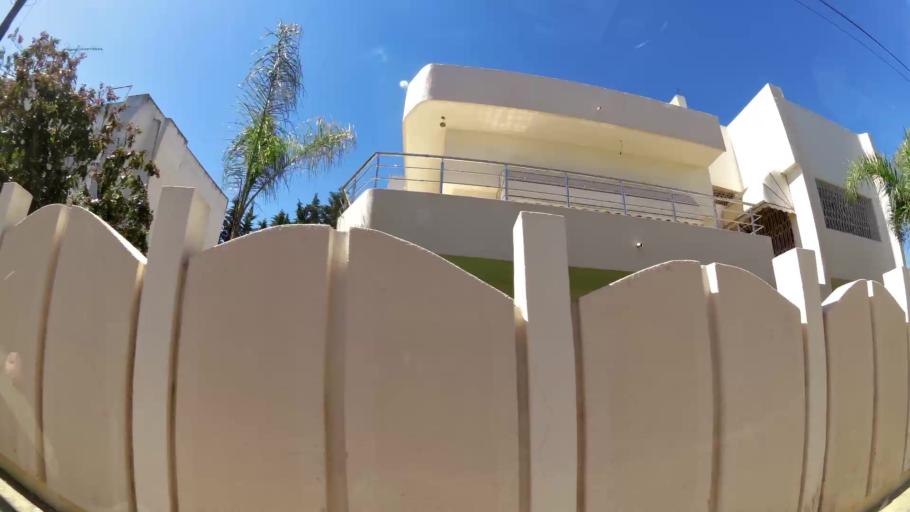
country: MA
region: Fes-Boulemane
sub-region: Fes
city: Fes
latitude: 34.0207
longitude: -4.9986
